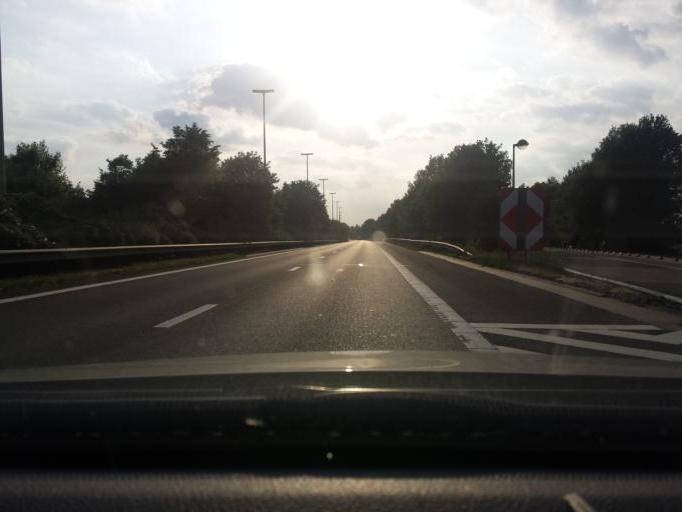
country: BE
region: Flanders
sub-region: Provincie Limburg
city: Diepenbeek
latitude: 50.8952
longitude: 5.4054
